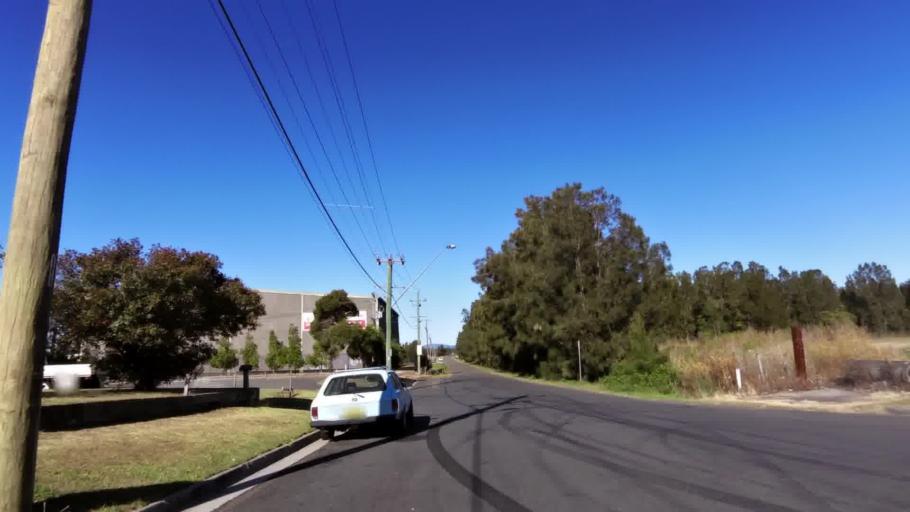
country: AU
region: New South Wales
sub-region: Wollongong
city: Berkeley
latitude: -34.4776
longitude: 150.8341
